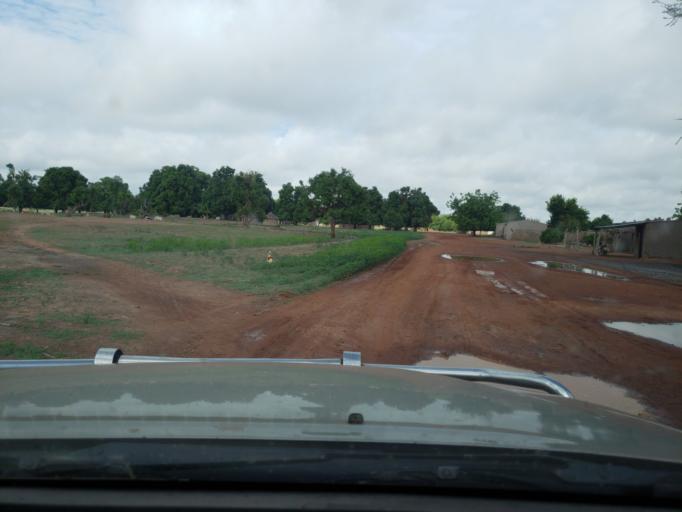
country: ML
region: Sikasso
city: Koutiala
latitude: 12.3921
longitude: -6.0238
